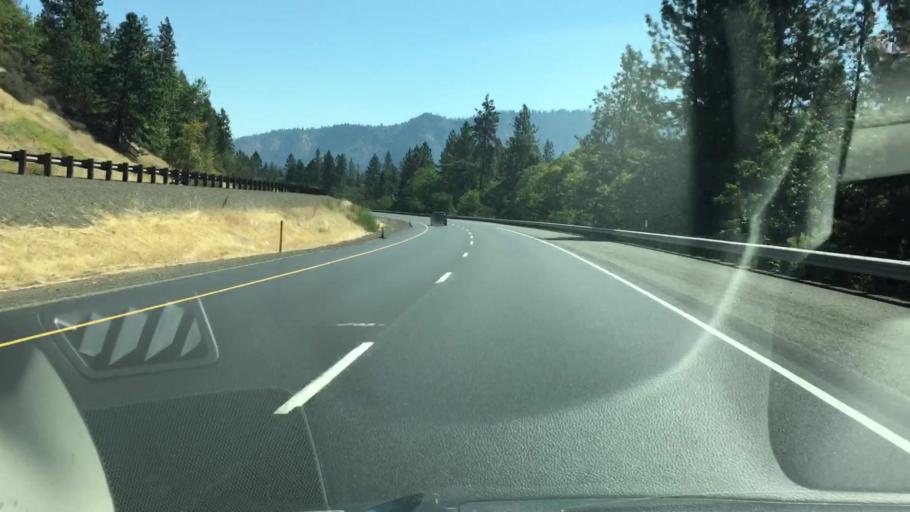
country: US
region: Oregon
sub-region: Josephine County
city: Fruitdale
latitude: 42.4278
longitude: -123.2480
